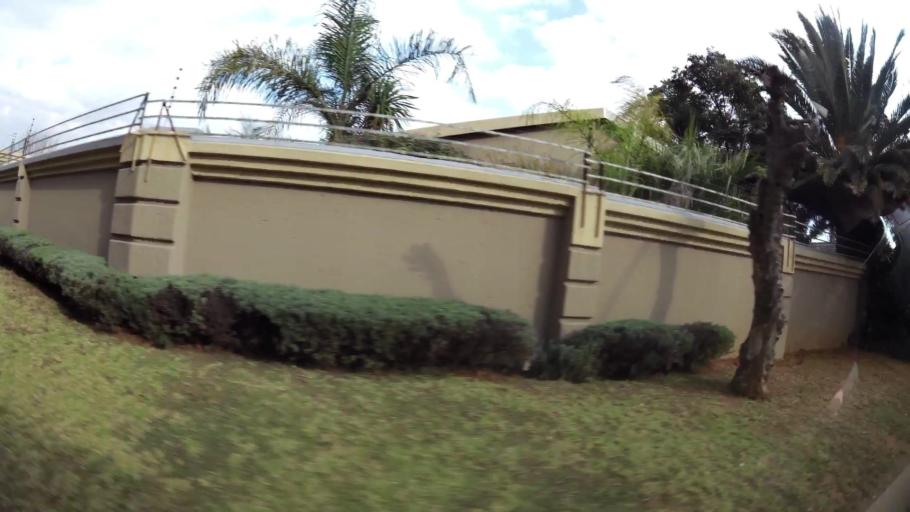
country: ZA
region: Gauteng
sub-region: Ekurhuleni Metropolitan Municipality
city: Benoni
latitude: -26.1191
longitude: 28.3757
